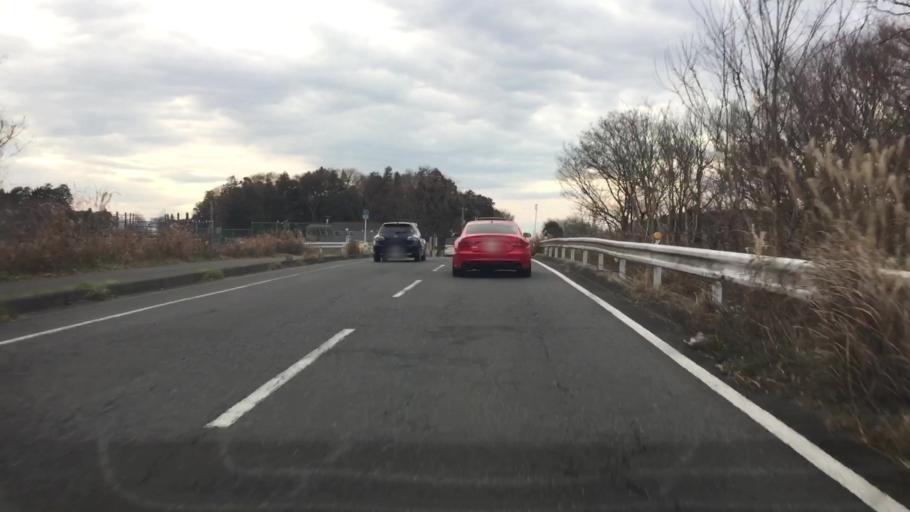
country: JP
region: Chiba
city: Shiroi
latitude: 35.7838
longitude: 140.0139
